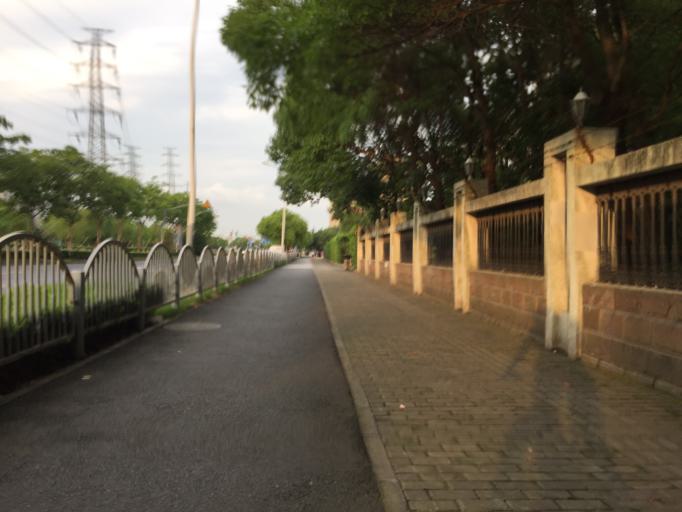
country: CN
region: Shanghai Shi
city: Huamu
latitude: 31.1896
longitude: 121.5393
